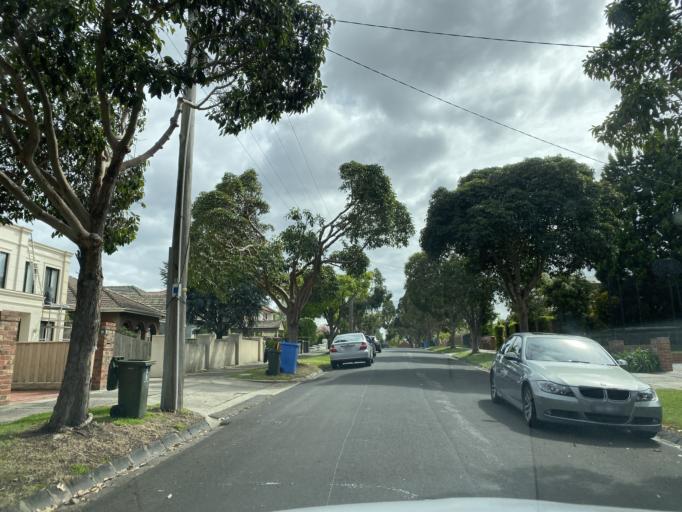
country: AU
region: Victoria
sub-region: Boroondara
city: Ashburton
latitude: -37.8543
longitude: 145.0773
